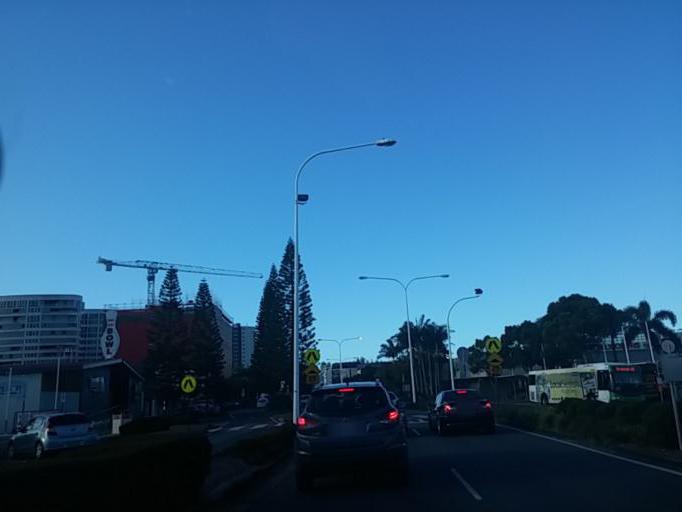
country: AU
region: New South Wales
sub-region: Tweed
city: Tweed Heads West
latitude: -28.1726
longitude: 153.5431
